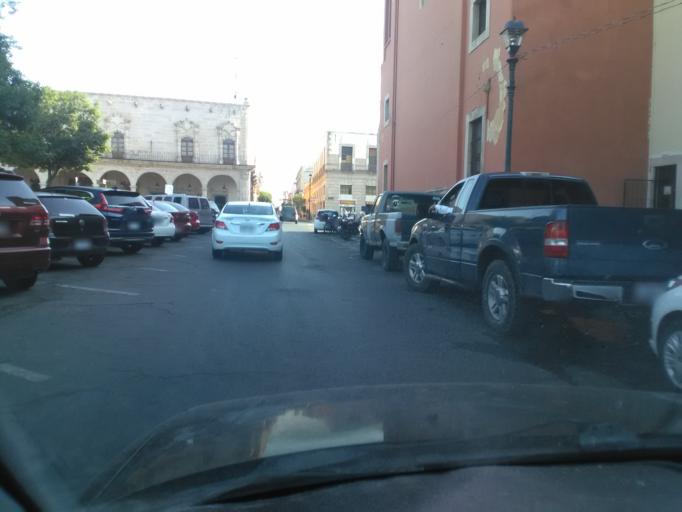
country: MX
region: Durango
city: Victoria de Durango
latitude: 24.0228
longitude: -104.6712
